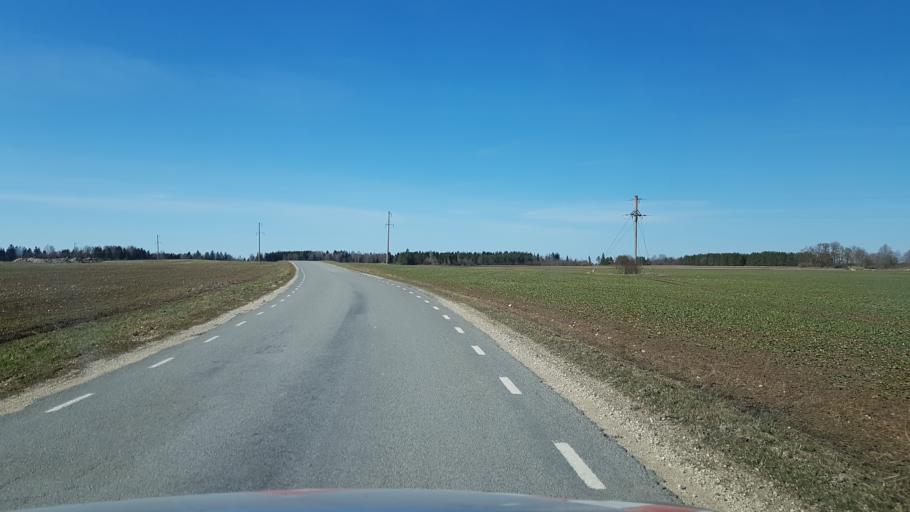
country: EE
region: Laeaene-Virumaa
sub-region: Someru vald
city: Someru
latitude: 59.3520
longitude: 26.4831
